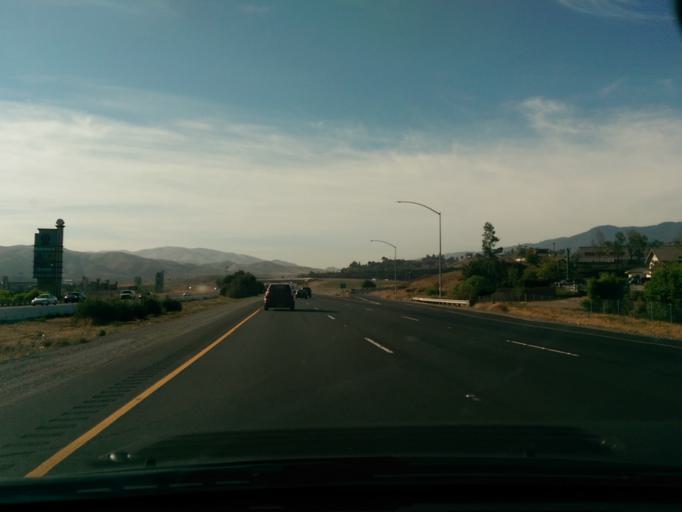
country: US
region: California
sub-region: Riverside County
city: El Cerrito
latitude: 33.8256
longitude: -117.5241
